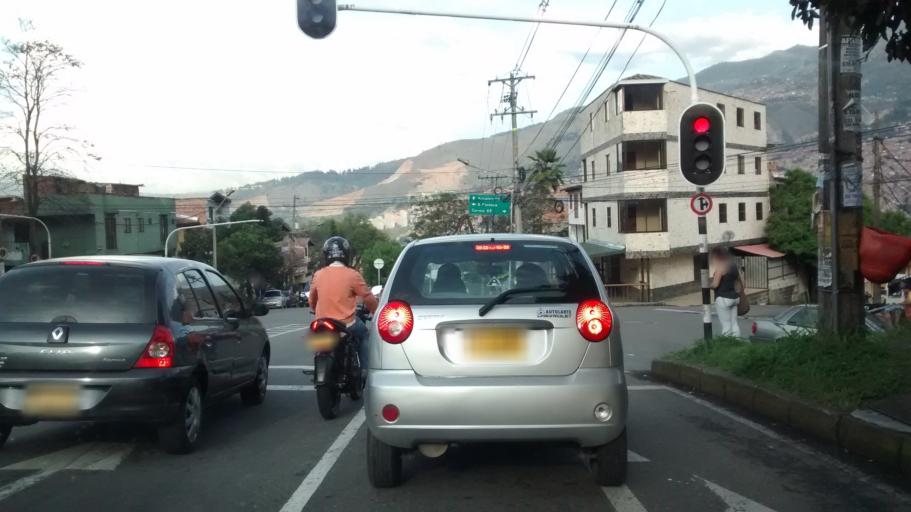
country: CO
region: Antioquia
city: Bello
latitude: 6.3009
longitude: -75.5675
